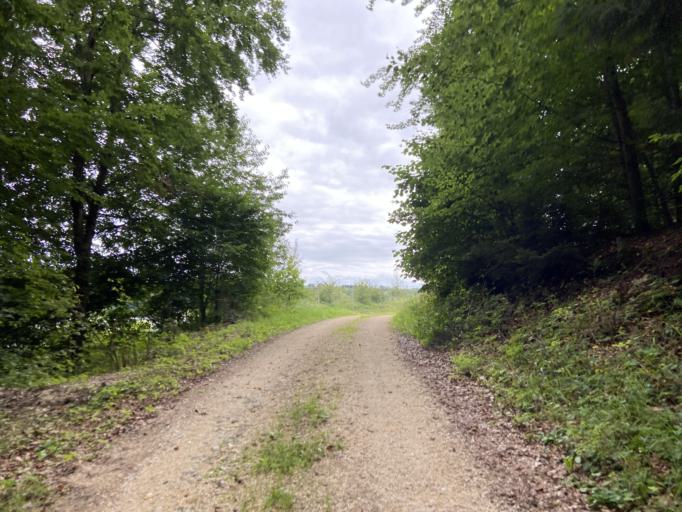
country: DE
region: Baden-Wuerttemberg
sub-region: Tuebingen Region
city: Sigmaringendorf
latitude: 48.0865
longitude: 9.2725
